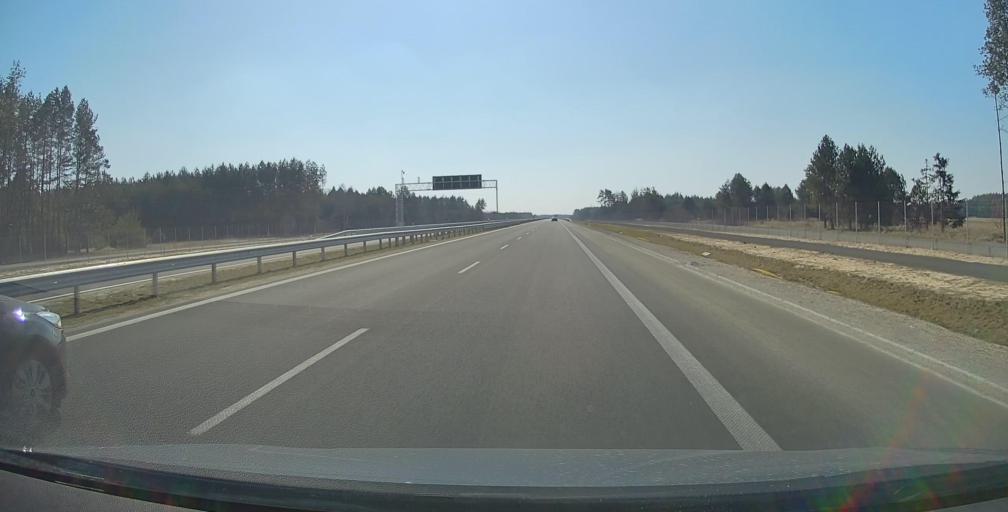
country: PL
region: Subcarpathian Voivodeship
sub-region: Powiat nizanski
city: Konczyce
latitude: 50.4575
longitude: 22.1409
